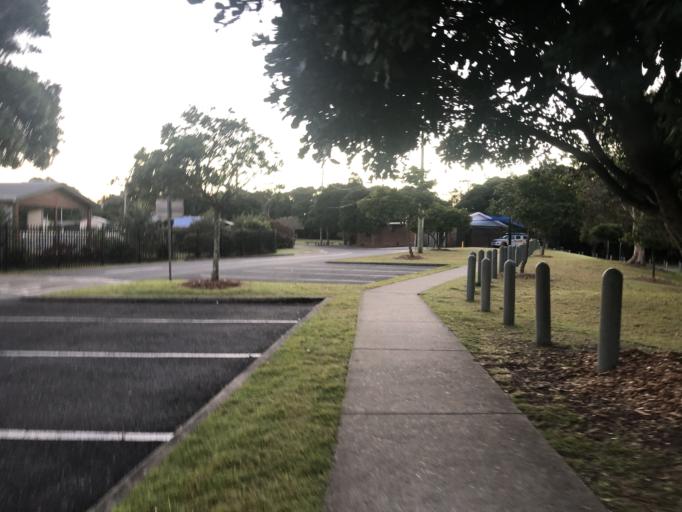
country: AU
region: New South Wales
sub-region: Coffs Harbour
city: Coffs Harbour
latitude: -30.2948
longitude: 153.1375
